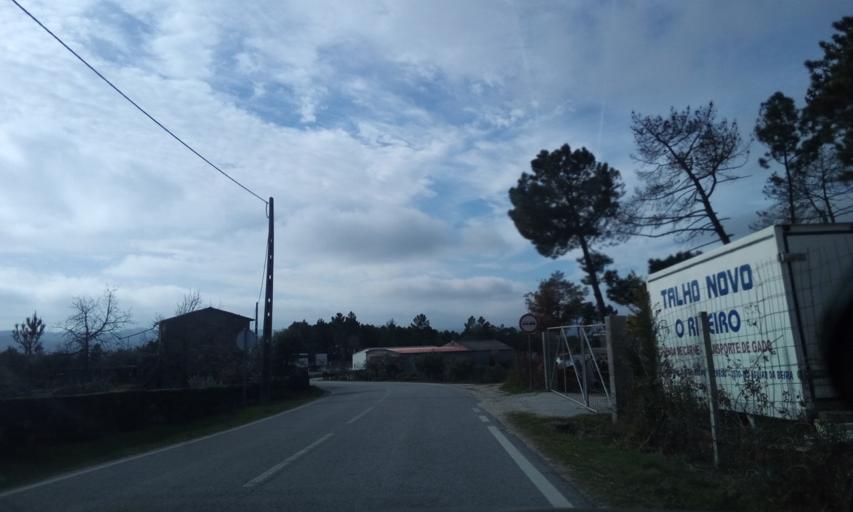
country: PT
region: Guarda
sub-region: Aguiar da Beira
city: Aguiar da Beira
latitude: 40.7439
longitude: -7.5550
